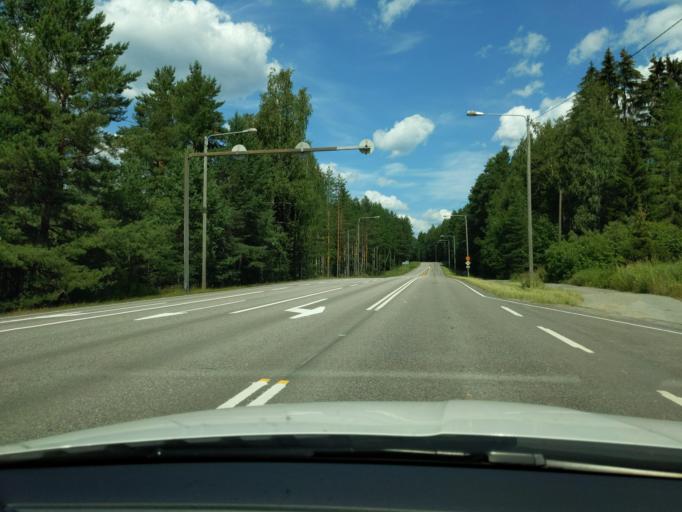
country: FI
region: Paijanne Tavastia
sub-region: Lahti
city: Heinola
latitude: 61.2490
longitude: 26.0595
